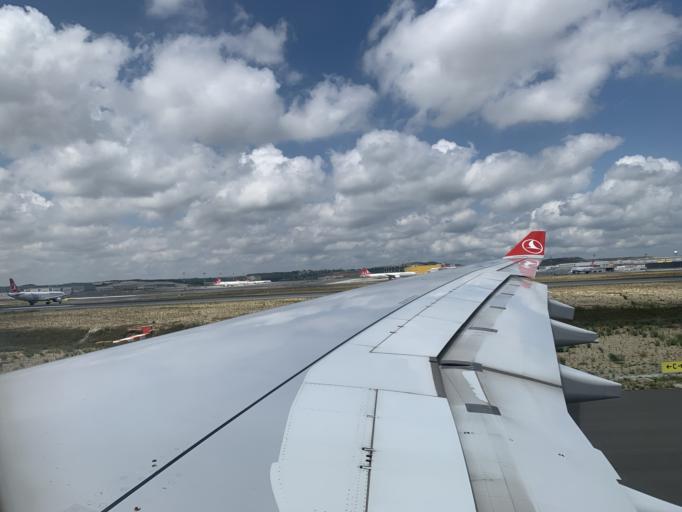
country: TR
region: Istanbul
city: Durusu
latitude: 41.2684
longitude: 28.7297
